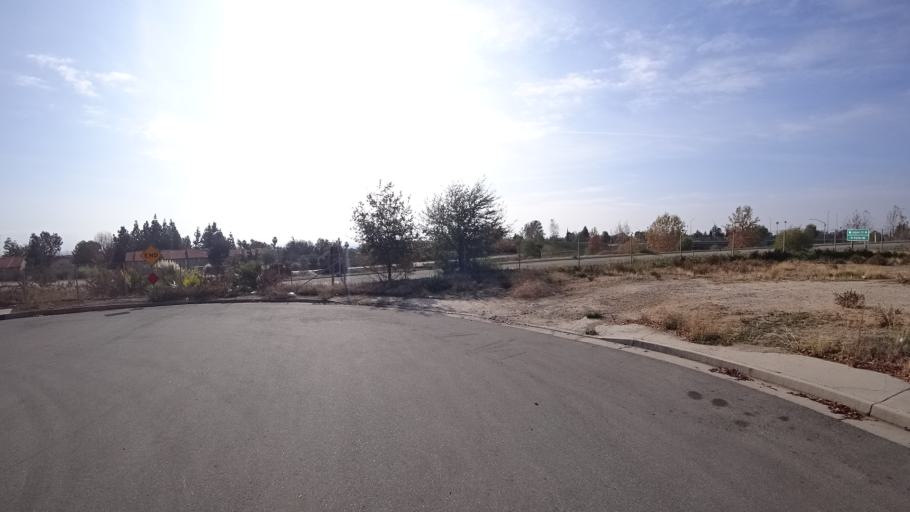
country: US
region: California
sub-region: Kern County
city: Bakersfield
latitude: 35.3972
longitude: -118.9276
